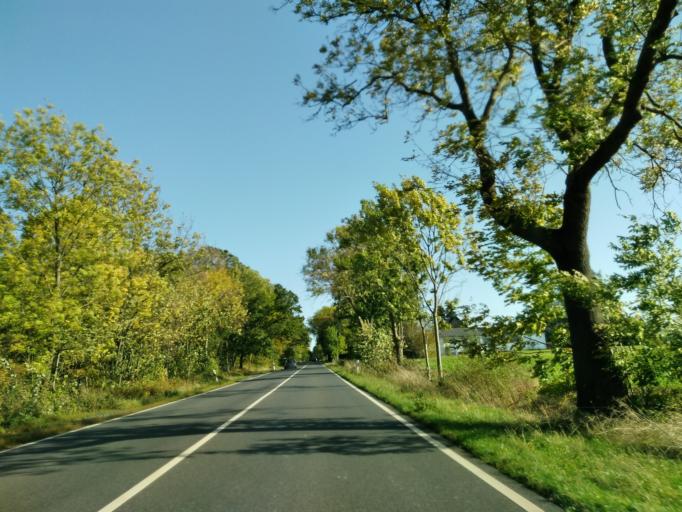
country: DE
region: Rheinland-Pfalz
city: Asbach
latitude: 50.7212
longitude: 7.3812
